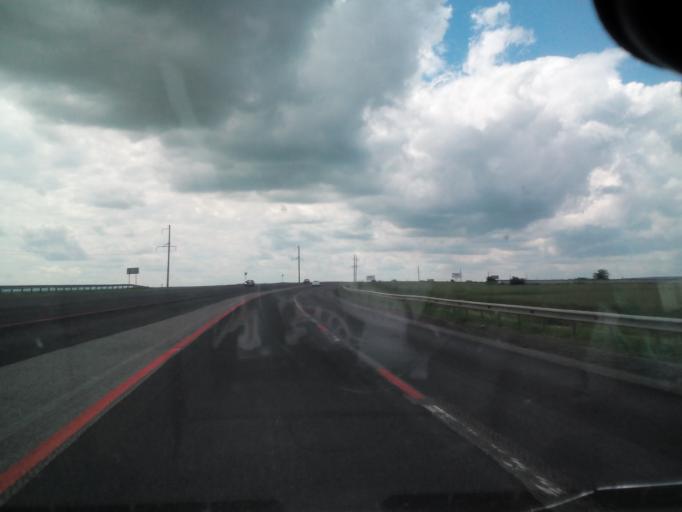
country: RU
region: Stavropol'skiy
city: Tatarka
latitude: 44.9547
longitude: 41.9868
